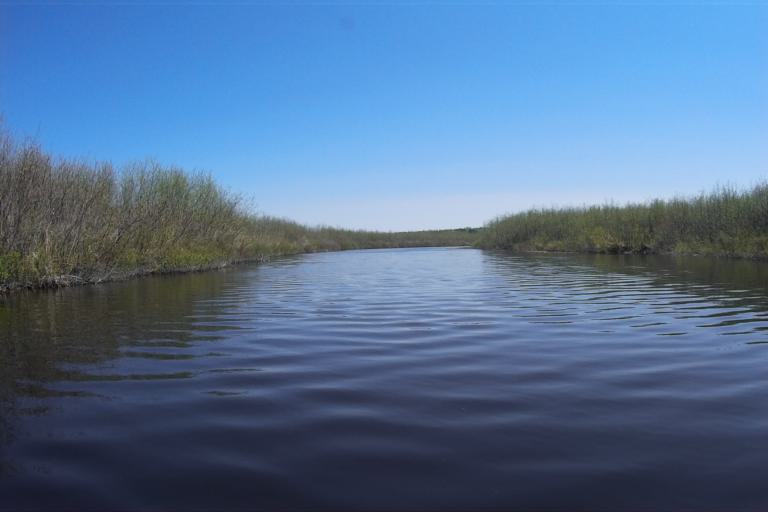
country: CA
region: Ontario
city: Powassan
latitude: 46.1604
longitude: -79.2573
